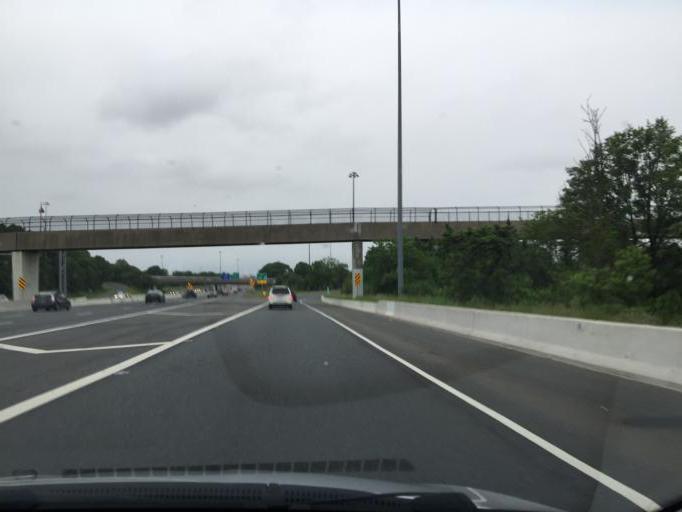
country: US
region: Maryland
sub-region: Baltimore County
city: Rosedale
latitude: 39.2921
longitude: -76.5325
